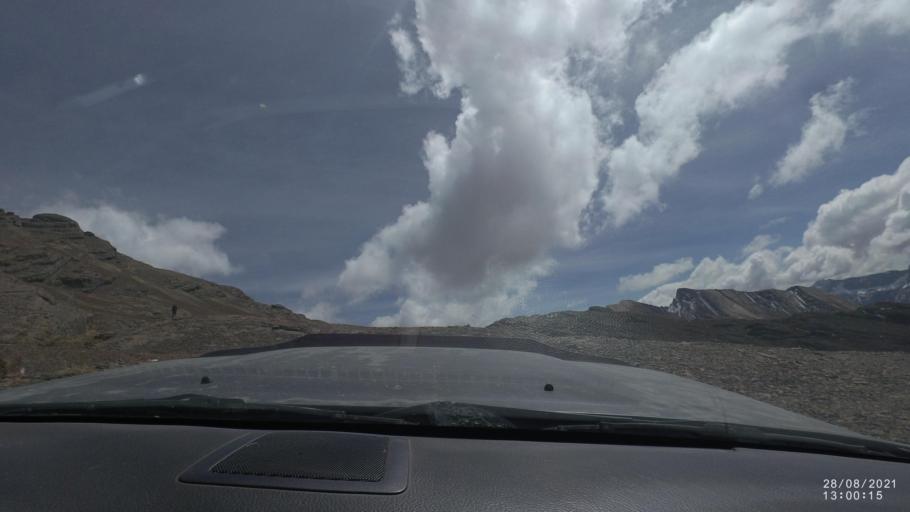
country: BO
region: Cochabamba
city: Sipe Sipe
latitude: -17.2836
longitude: -66.3857
